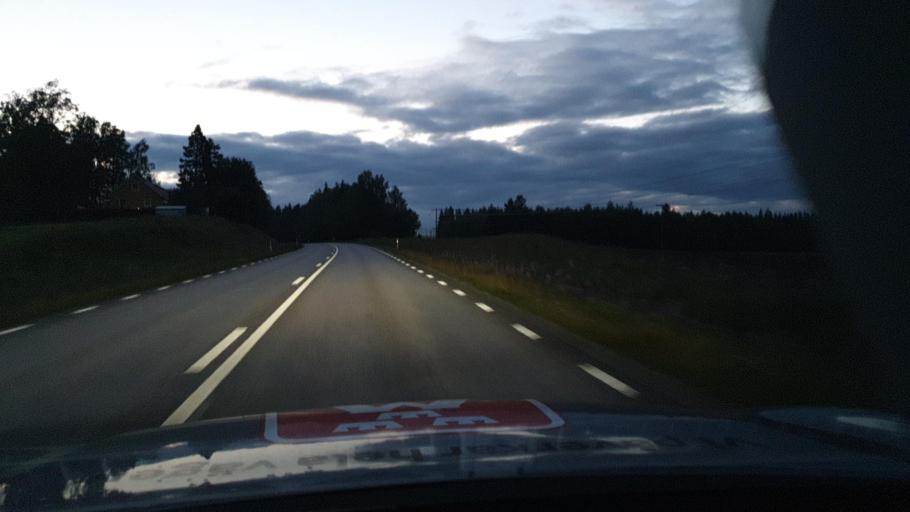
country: SE
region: OErebro
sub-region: Karlskoga Kommun
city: Karlskoga
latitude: 59.3588
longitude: 14.5114
